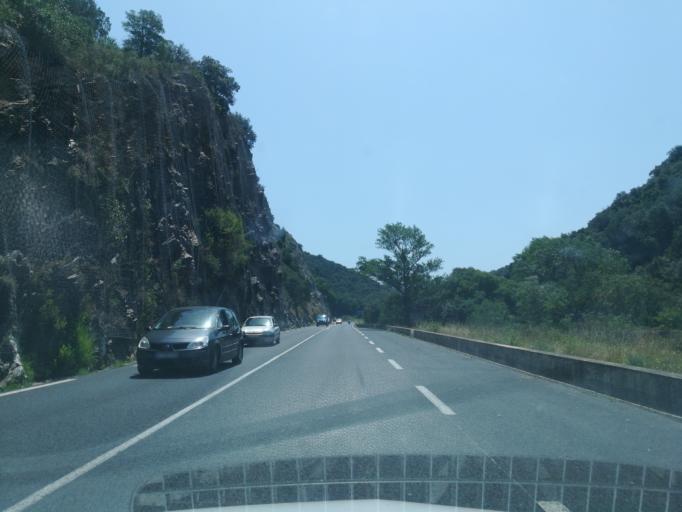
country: FR
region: Languedoc-Roussillon
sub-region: Departement des Pyrenees-Orientales
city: Maureillas-las-Illas
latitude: 42.4834
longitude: 2.8403
